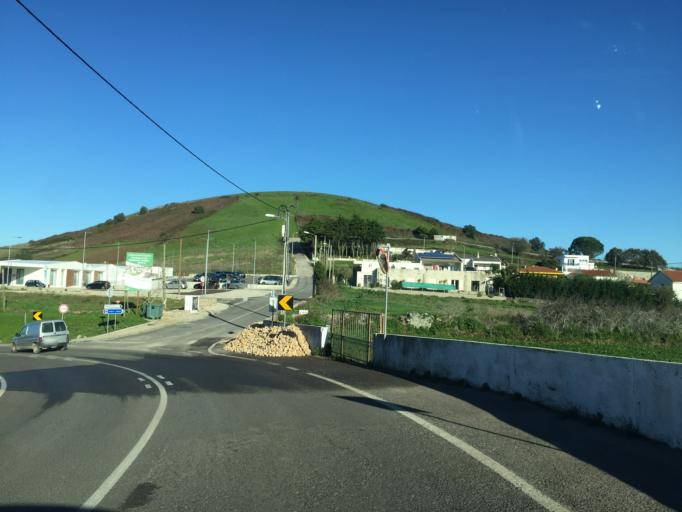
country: PT
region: Lisbon
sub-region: Sintra
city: Almargem
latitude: 38.8506
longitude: -9.2638
